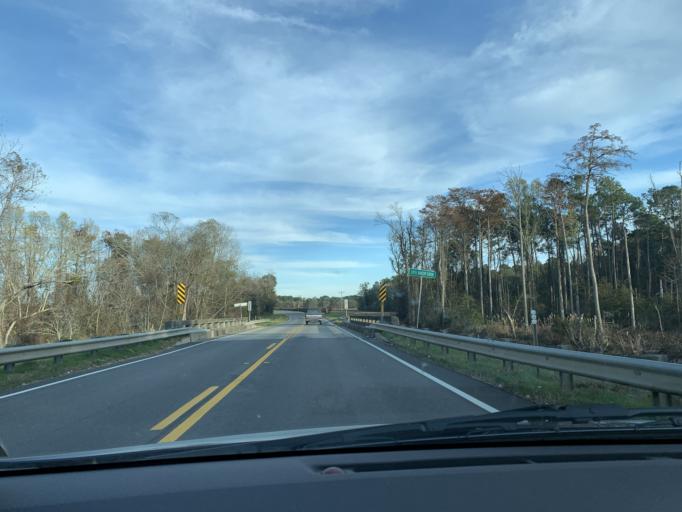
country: US
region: Georgia
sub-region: Irwin County
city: Ocilla
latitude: 31.5922
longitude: -83.2046
